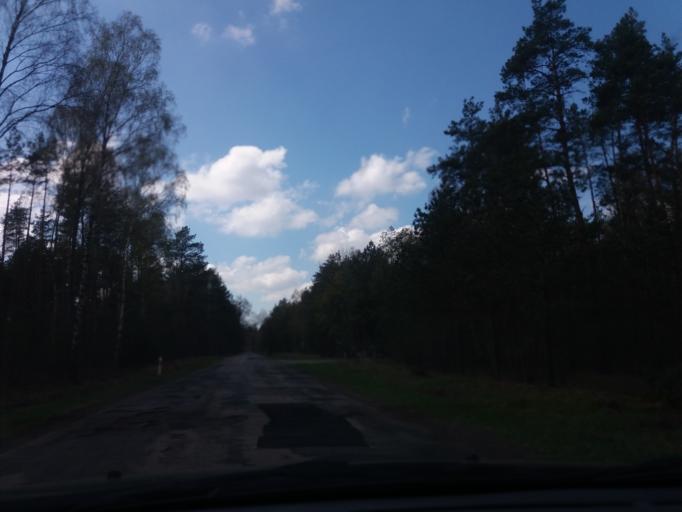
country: PL
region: Warmian-Masurian Voivodeship
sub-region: Powiat szczycienski
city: Jedwabno
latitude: 53.3626
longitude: 20.7059
